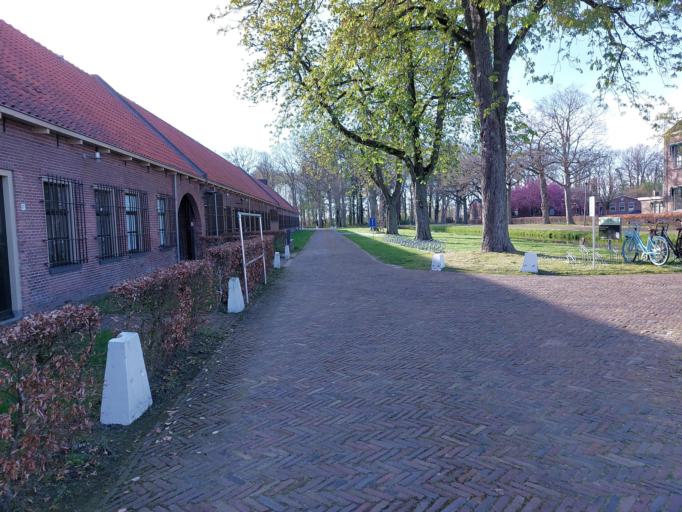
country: NL
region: Groningen
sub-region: Gemeente Leek
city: Leek
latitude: 53.0418
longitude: 6.3913
